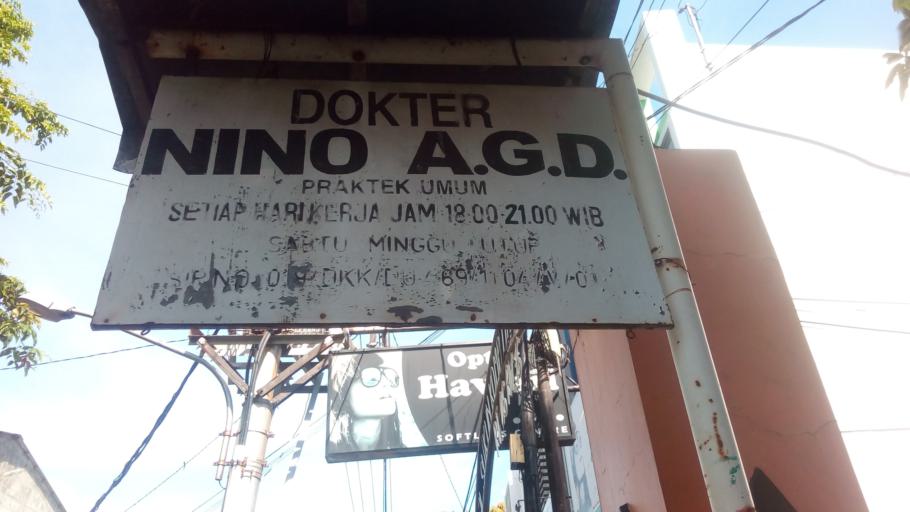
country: ID
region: Central Java
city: Semarang
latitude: -7.0661
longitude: 110.4178
